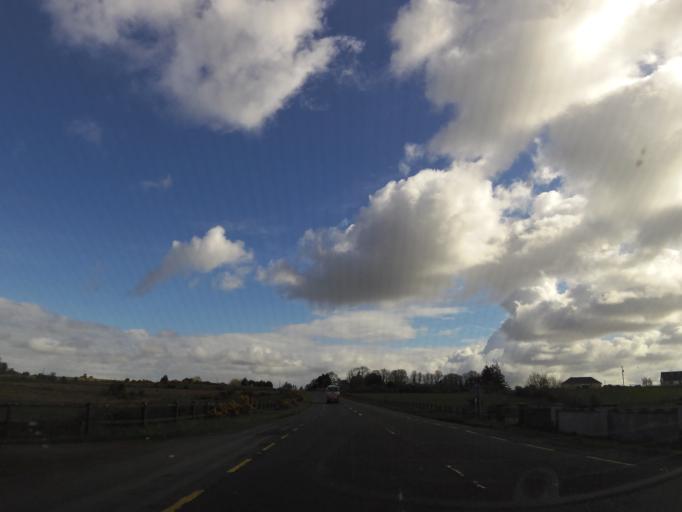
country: IE
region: Connaught
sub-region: Maigh Eo
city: Ballyhaunis
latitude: 53.8335
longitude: -8.8637
